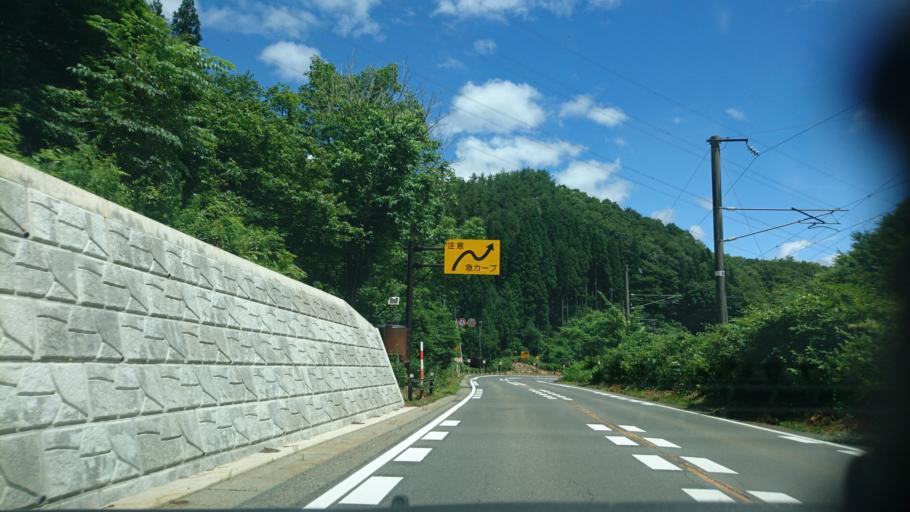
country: JP
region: Akita
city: Kakunodatemachi
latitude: 39.6769
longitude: 140.6999
